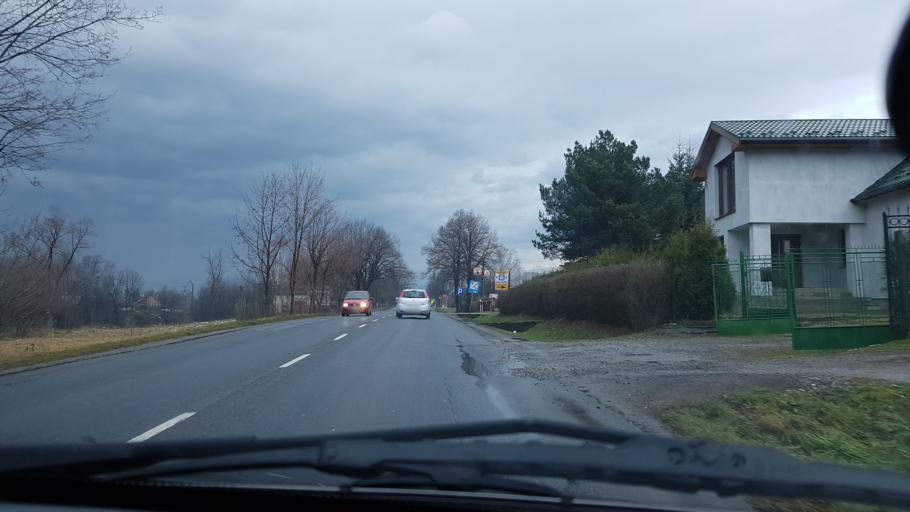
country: PL
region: Silesian Voivodeship
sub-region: Powiat zywiecki
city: Lodygowice
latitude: 49.7215
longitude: 19.1441
